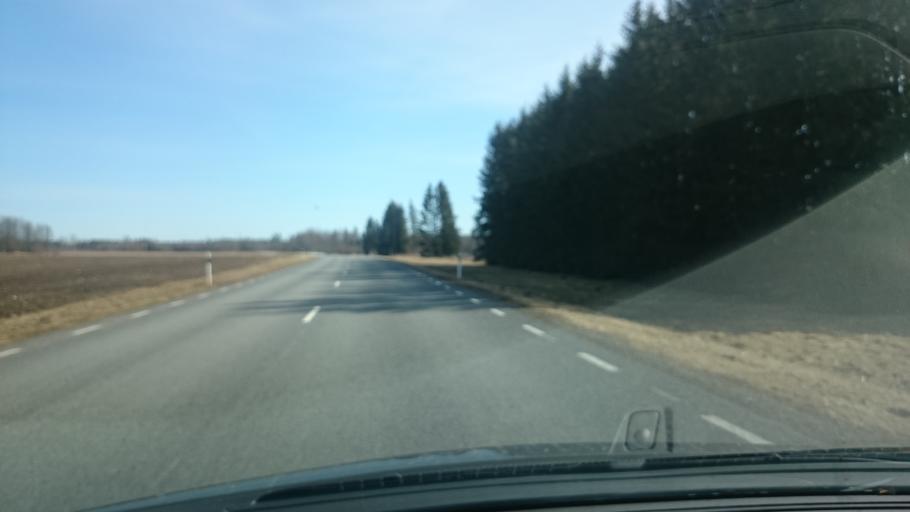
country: EE
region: Paernumaa
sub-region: Tootsi vald
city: Tootsi
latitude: 58.6657
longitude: 24.7860
